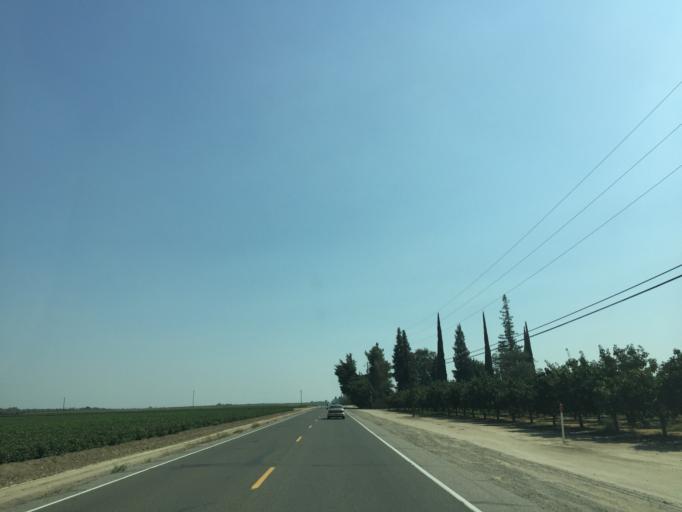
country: US
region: California
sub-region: Kings County
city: Lucerne
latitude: 36.3972
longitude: -119.6730
